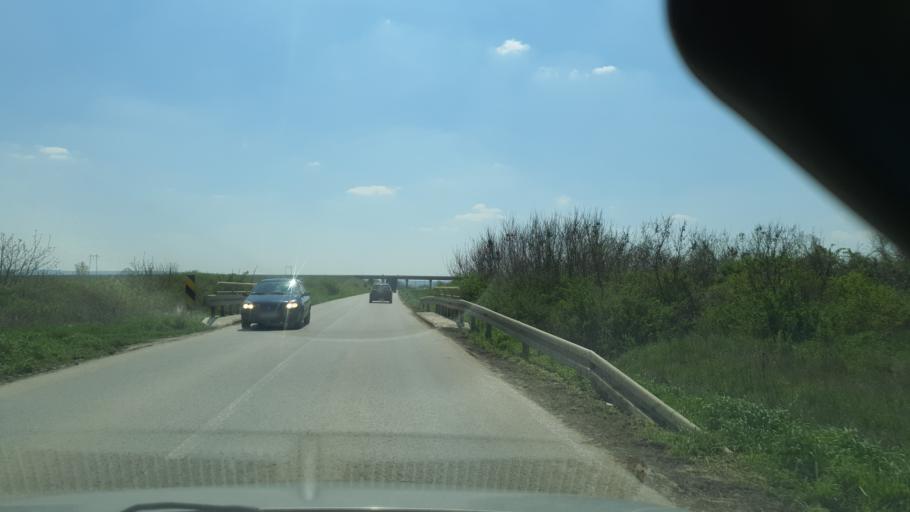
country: RS
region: Autonomna Pokrajina Vojvodina
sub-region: Juznobacki Okrug
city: Backa Palanka
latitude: 45.2806
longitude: 19.4217
